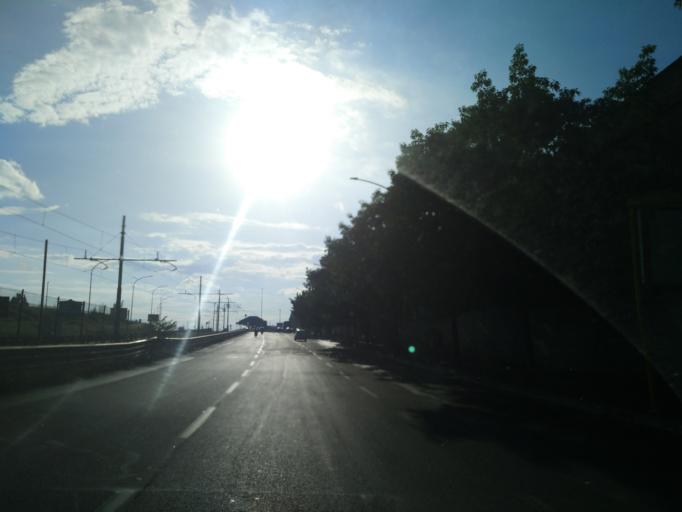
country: IT
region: Latium
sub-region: Citta metropolitana di Roma Capitale
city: Rome
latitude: 41.8746
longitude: 12.5673
